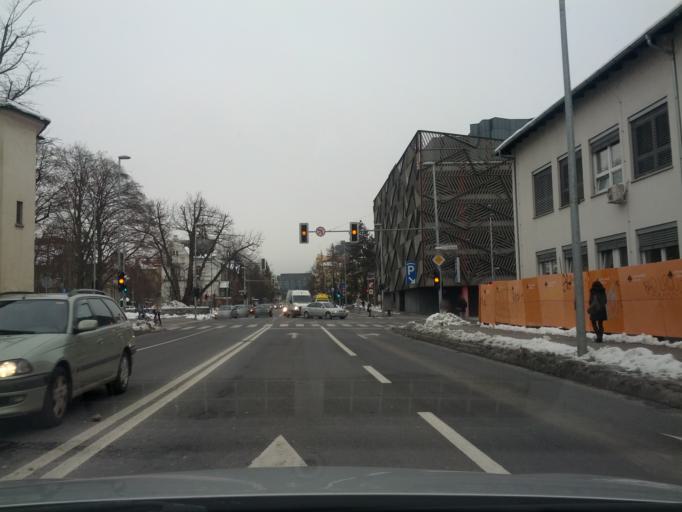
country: SI
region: Ljubljana
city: Ljubljana
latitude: 46.0516
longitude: 14.5193
